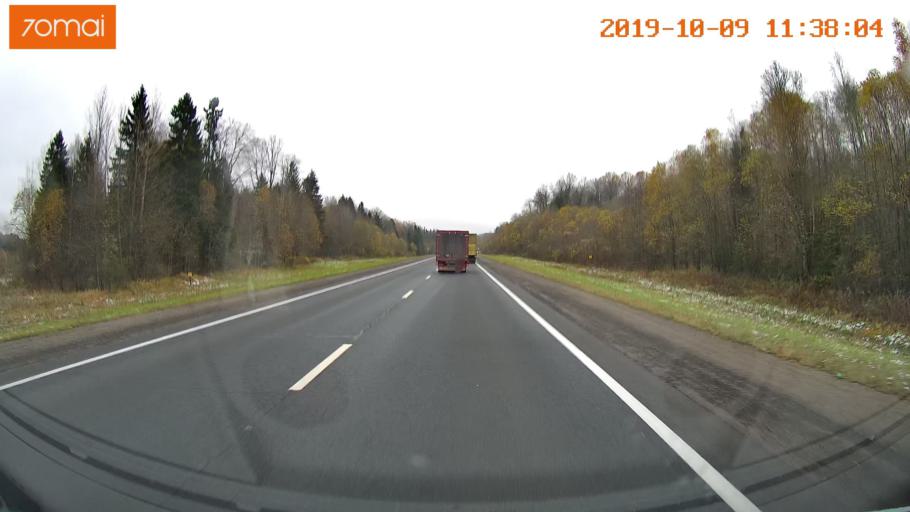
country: RU
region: Vologda
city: Gryazovets
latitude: 58.9721
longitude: 40.1525
